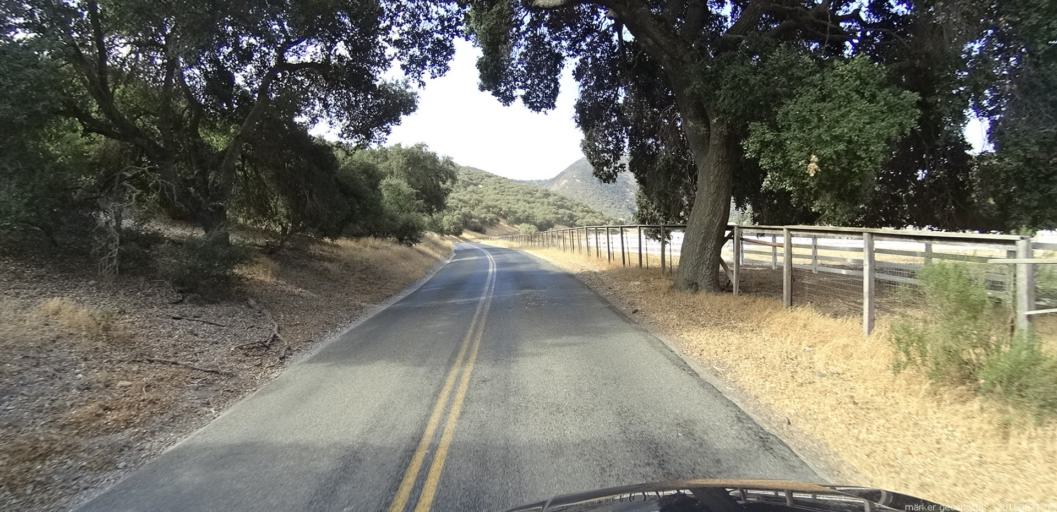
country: US
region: California
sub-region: Monterey County
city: King City
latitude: 36.1628
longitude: -121.1627
